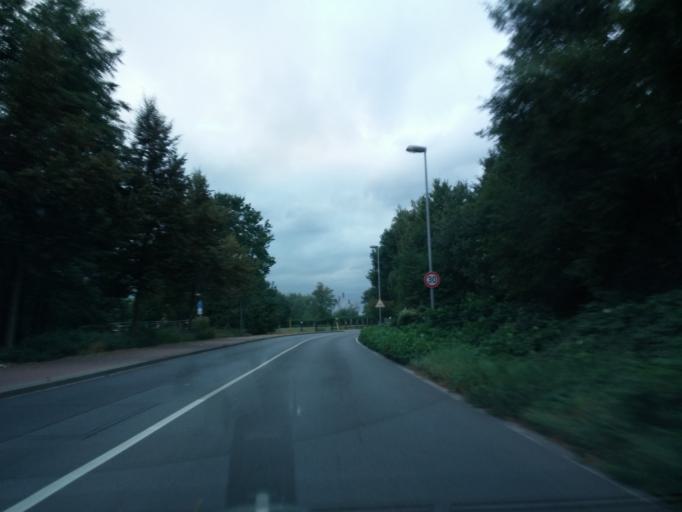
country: DE
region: North Rhine-Westphalia
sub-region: Regierungsbezirk Munster
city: Gladbeck
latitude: 51.5664
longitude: 7.0281
